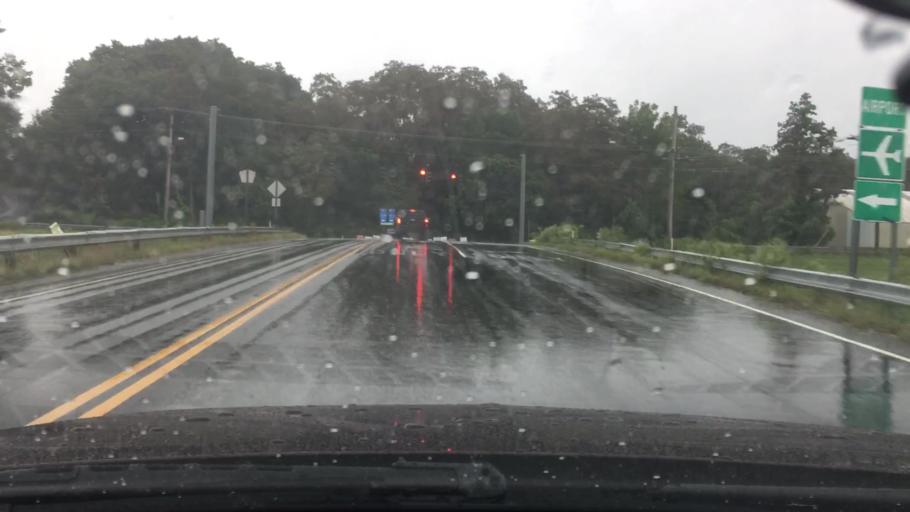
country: US
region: New York
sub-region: Dutchess County
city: Myers Corner
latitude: 41.6205
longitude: -73.8918
